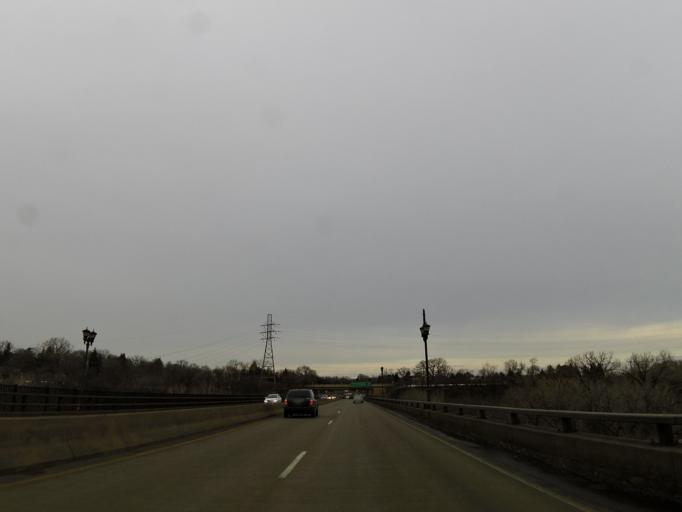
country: US
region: Minnesota
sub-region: Dakota County
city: Mendota Heights
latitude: 44.8944
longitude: -93.1815
